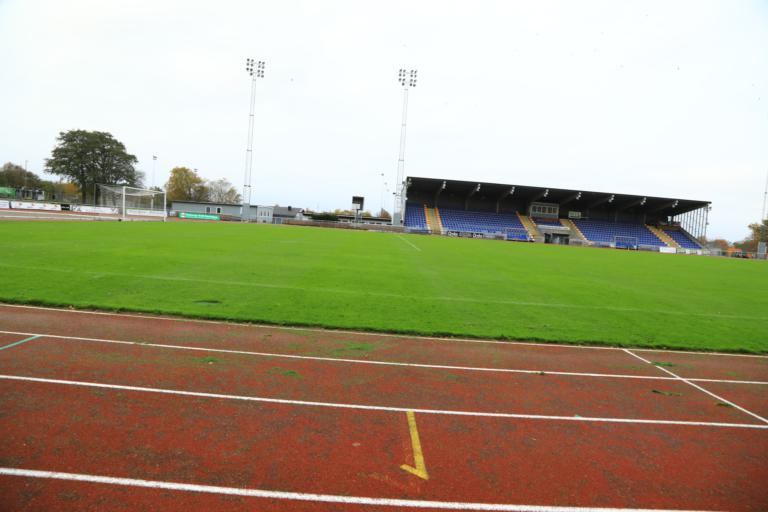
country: SE
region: Halland
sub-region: Varbergs Kommun
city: Varberg
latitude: 57.0982
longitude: 12.2663
